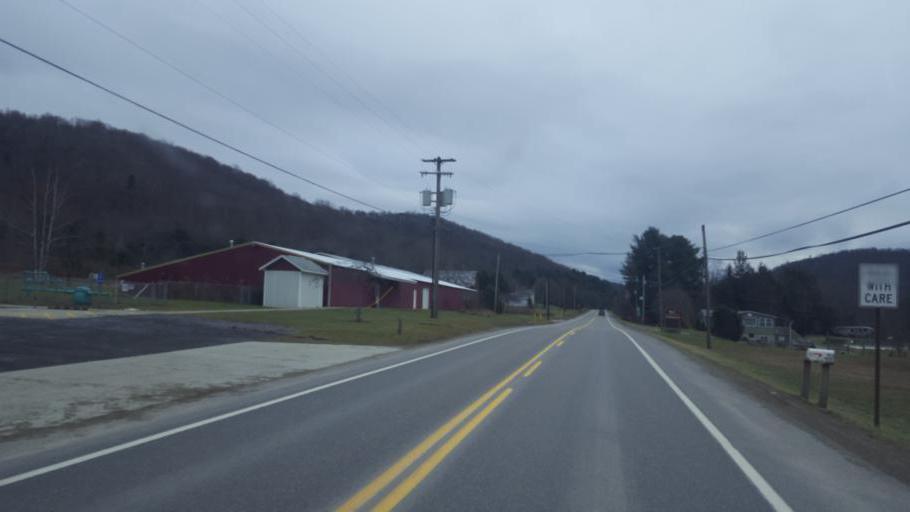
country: US
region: Pennsylvania
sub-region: Potter County
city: Coudersport
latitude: 41.7621
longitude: -78.1150
